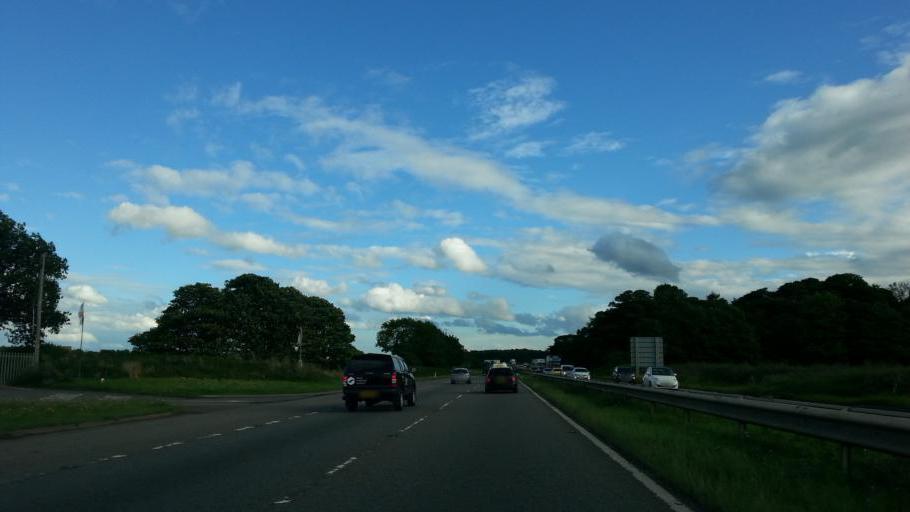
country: GB
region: England
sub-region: Nottinghamshire
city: Bircotes
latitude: 53.3649
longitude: -1.0523
